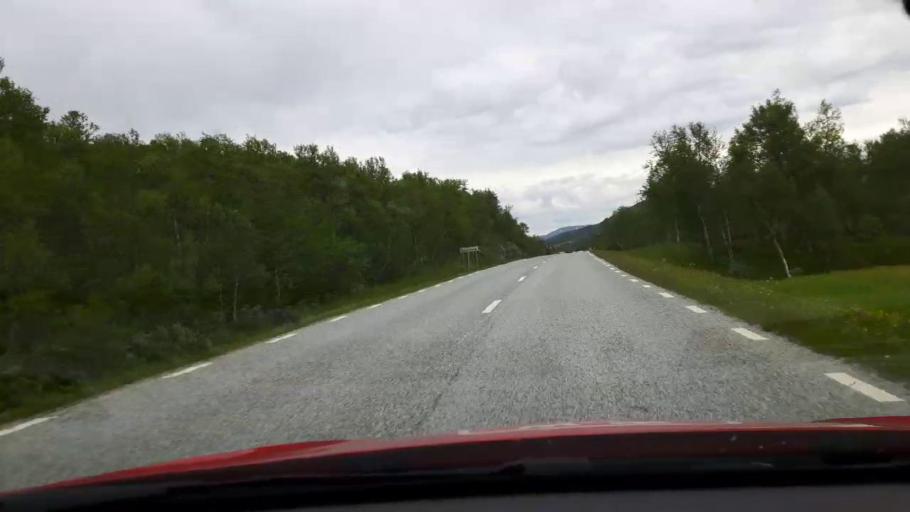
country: NO
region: Sor-Trondelag
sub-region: Tydal
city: Aas
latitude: 62.5913
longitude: 12.1907
